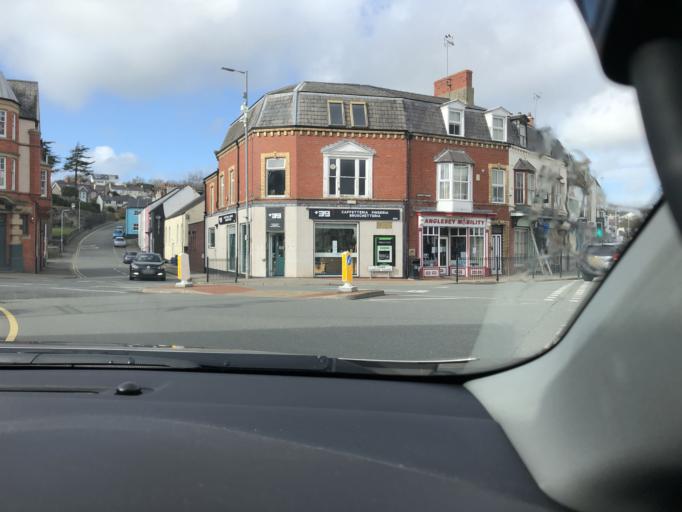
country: GB
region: Wales
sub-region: Anglesey
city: Menai Bridge
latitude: 53.2257
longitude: -4.1629
